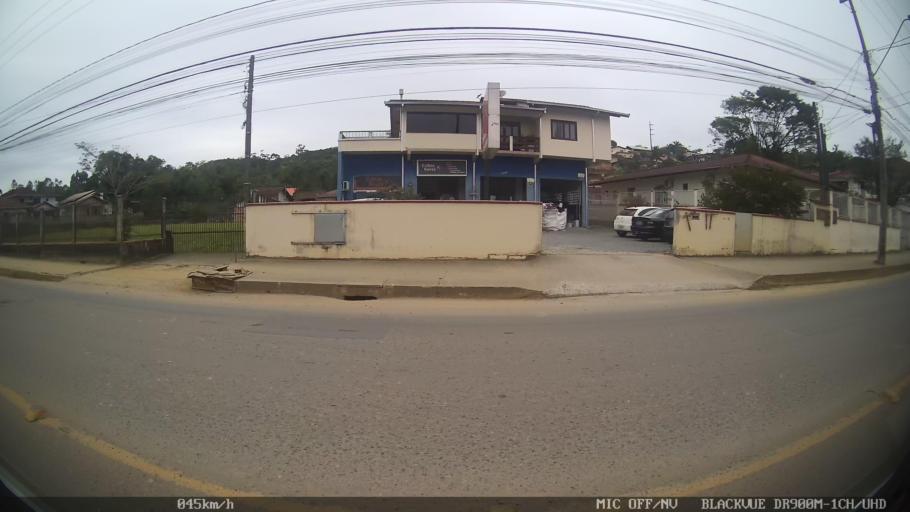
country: BR
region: Santa Catarina
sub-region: Joinville
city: Joinville
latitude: -26.3617
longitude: -48.8181
